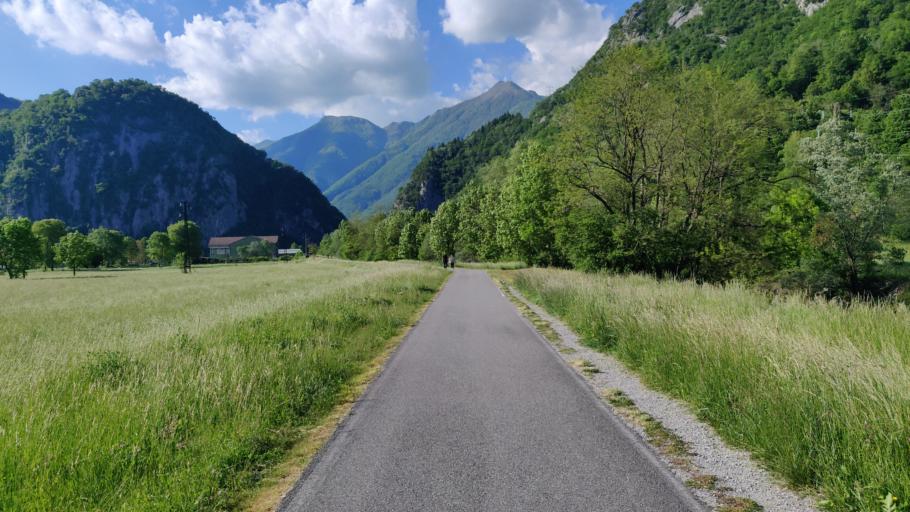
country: IT
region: Lombardy
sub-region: Provincia di Lecco
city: Pasturo
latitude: 45.9532
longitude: 9.4529
